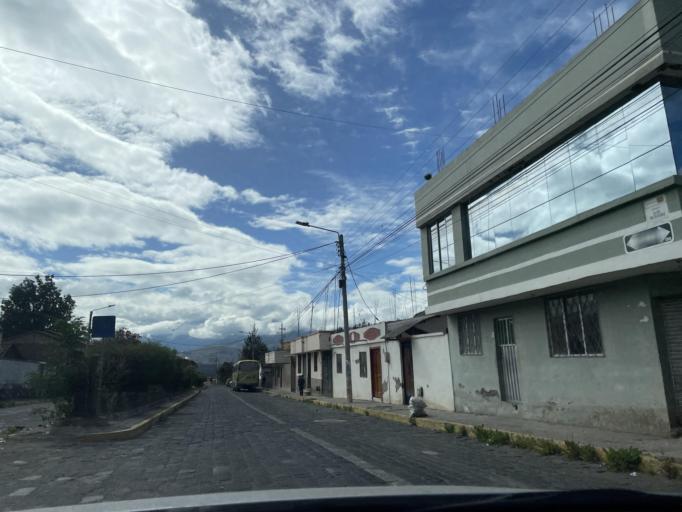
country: EC
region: Chimborazo
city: Guano
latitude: -1.6085
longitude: -78.6366
